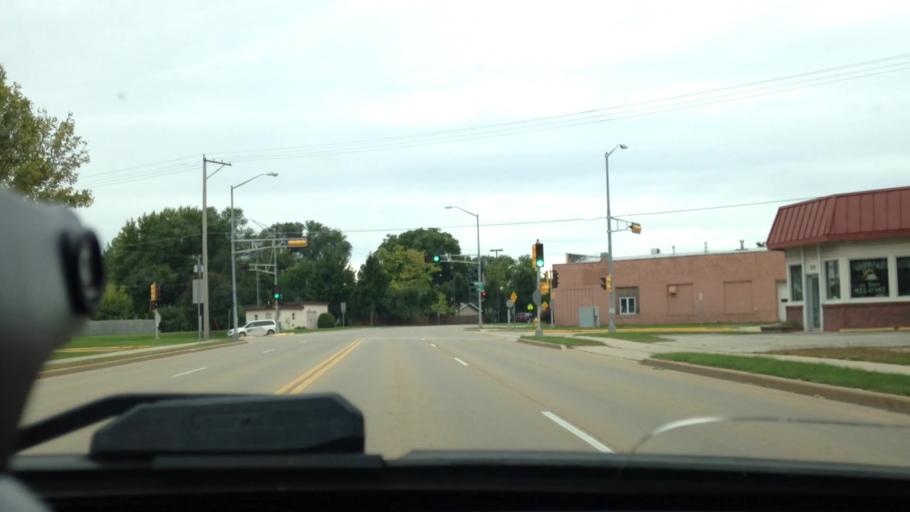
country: US
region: Wisconsin
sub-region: Fond du Lac County
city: North Fond du Lac
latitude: 43.8059
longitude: -88.4830
